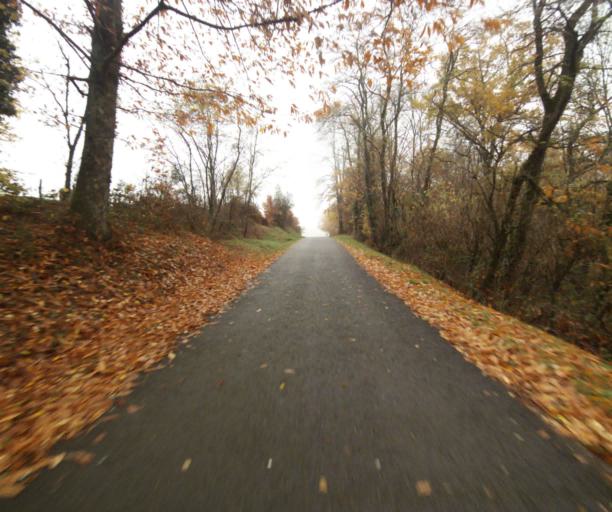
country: FR
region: Limousin
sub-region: Departement de la Correze
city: Cornil
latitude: 45.2006
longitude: 1.6400
